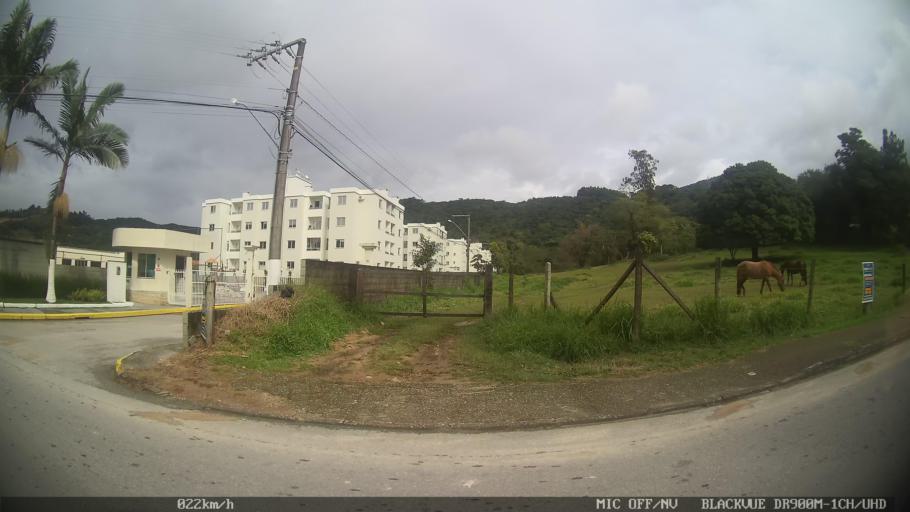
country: BR
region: Santa Catarina
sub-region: Biguacu
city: Biguacu
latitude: -27.5219
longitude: -48.6568
